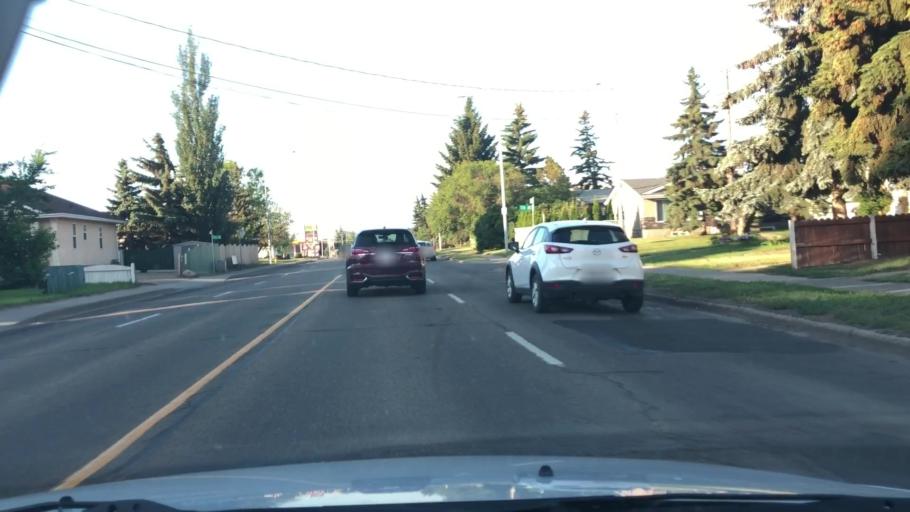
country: CA
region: Alberta
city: Edmonton
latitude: 53.5950
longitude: -113.5412
